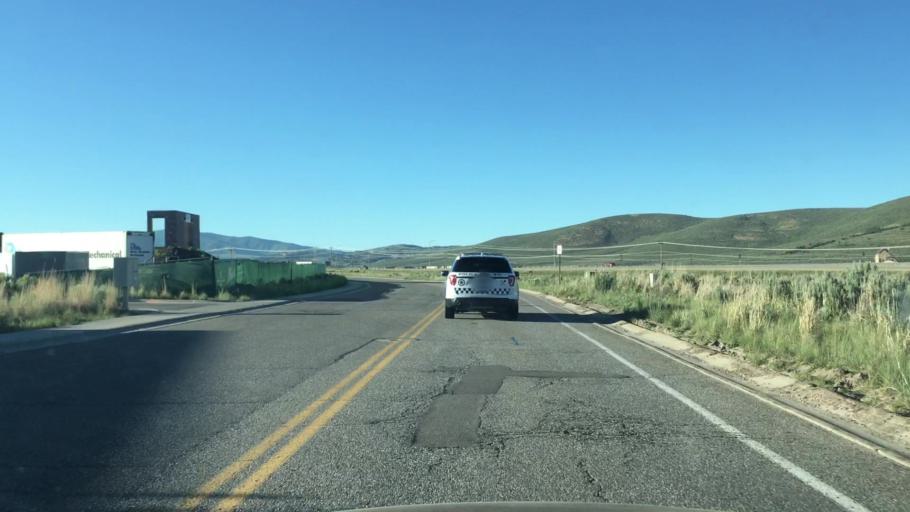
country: US
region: Utah
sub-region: Summit County
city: Park City
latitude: 40.6839
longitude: -111.4662
